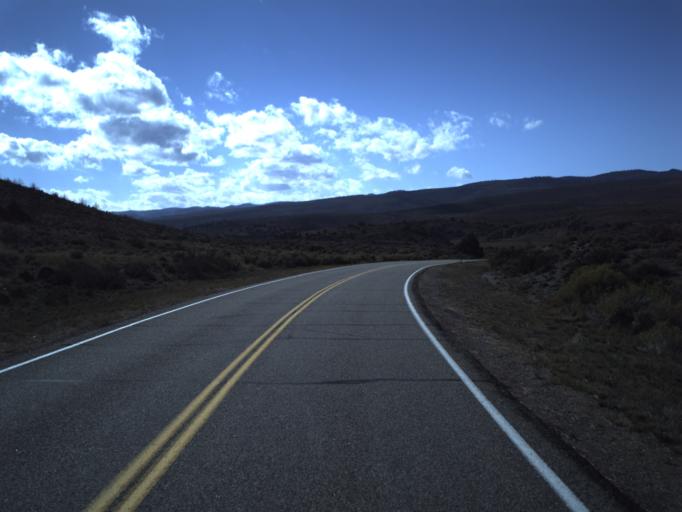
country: US
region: Utah
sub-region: Garfield County
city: Panguitch
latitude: 37.7672
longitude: -112.5410
